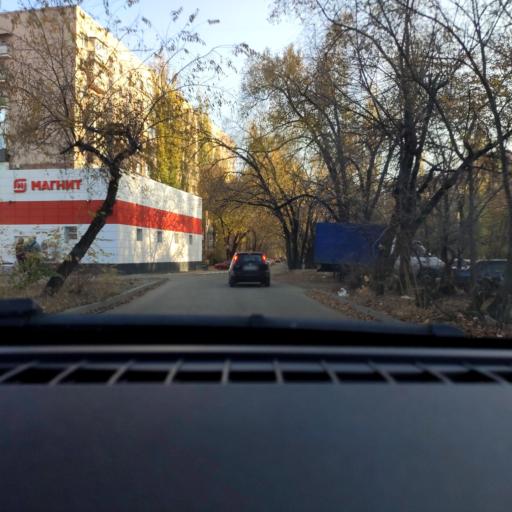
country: RU
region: Voronezj
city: Voronezh
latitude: 51.7102
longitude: 39.2716
